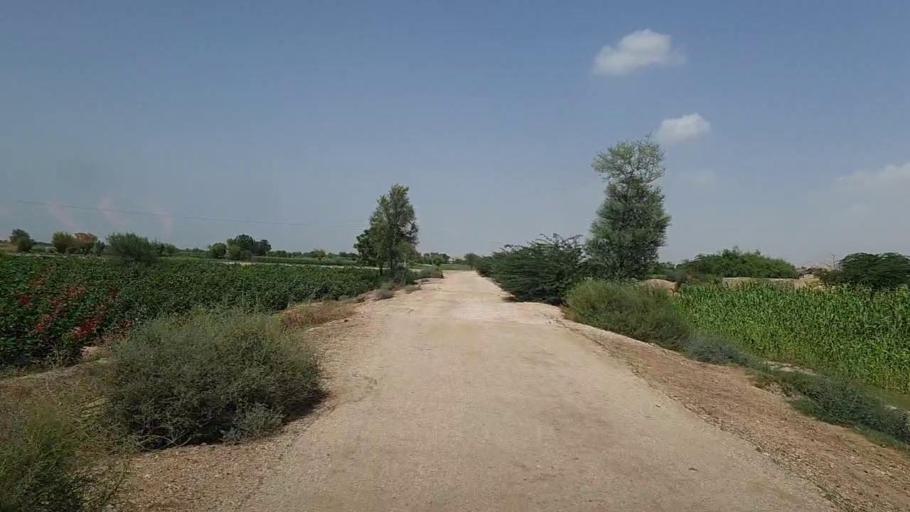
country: PK
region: Sindh
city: Pad Idan
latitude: 26.8003
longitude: 68.3681
